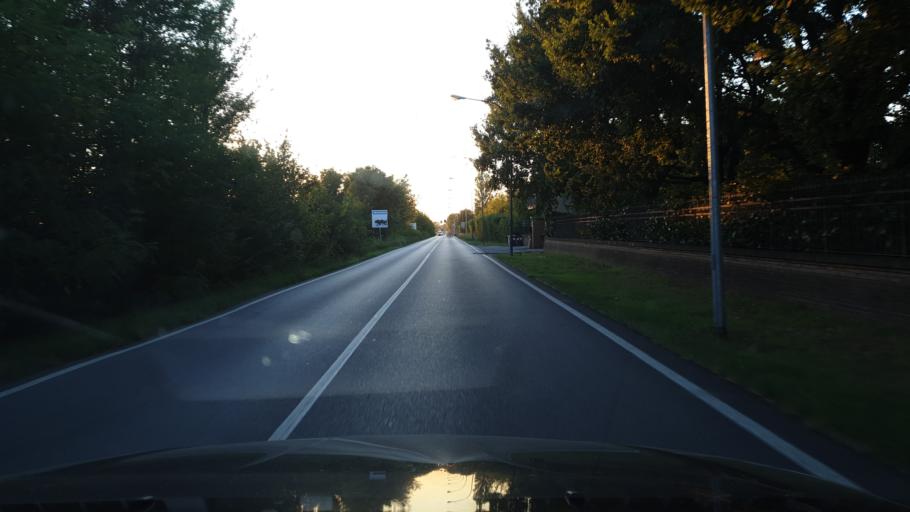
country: IT
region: Emilia-Romagna
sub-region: Provincia di Bologna
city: Quarto Inferiore
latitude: 44.5279
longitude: 11.3878
